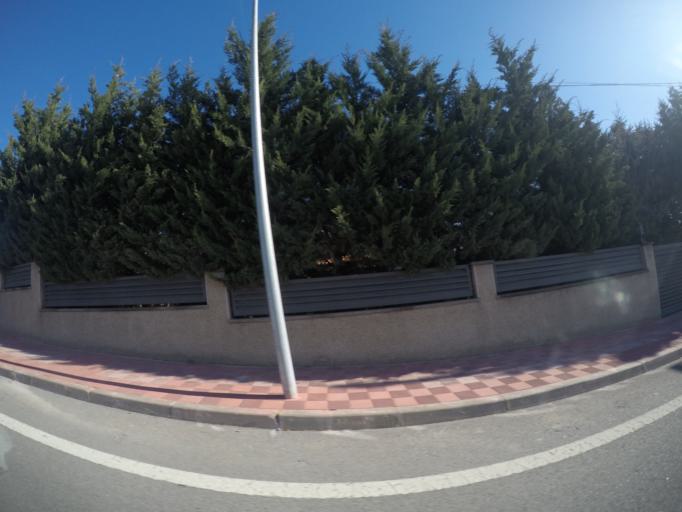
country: ES
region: Catalonia
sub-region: Provincia de Barcelona
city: Collbato
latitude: 41.5660
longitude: 1.8106
